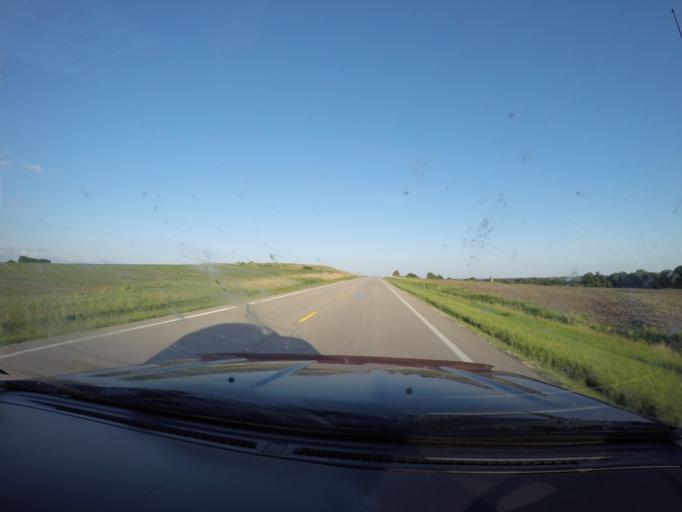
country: US
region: Kansas
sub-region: Marshall County
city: Blue Rapids
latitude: 39.7030
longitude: -96.8593
